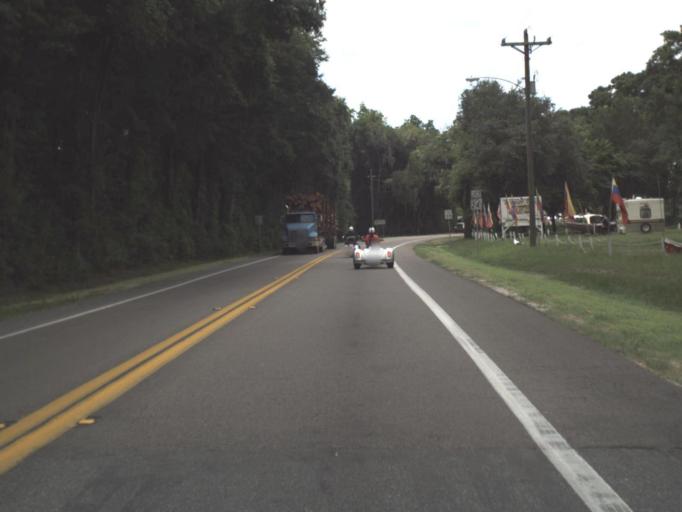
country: US
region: Florida
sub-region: Alachua County
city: Archer
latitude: 29.5397
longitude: -82.5198
